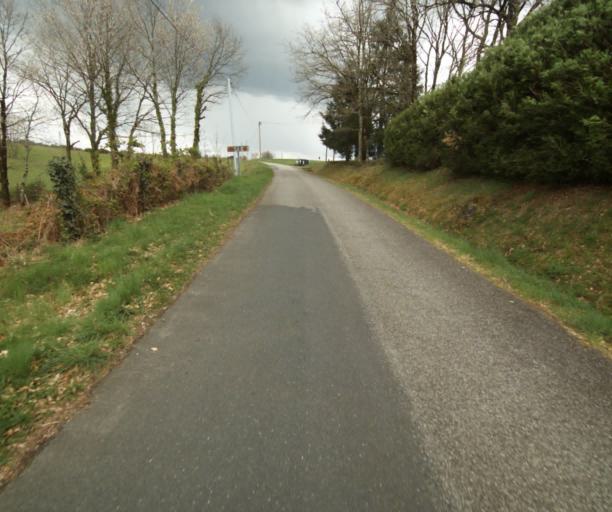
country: FR
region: Limousin
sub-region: Departement de la Correze
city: Naves
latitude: 45.3073
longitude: 1.8120
